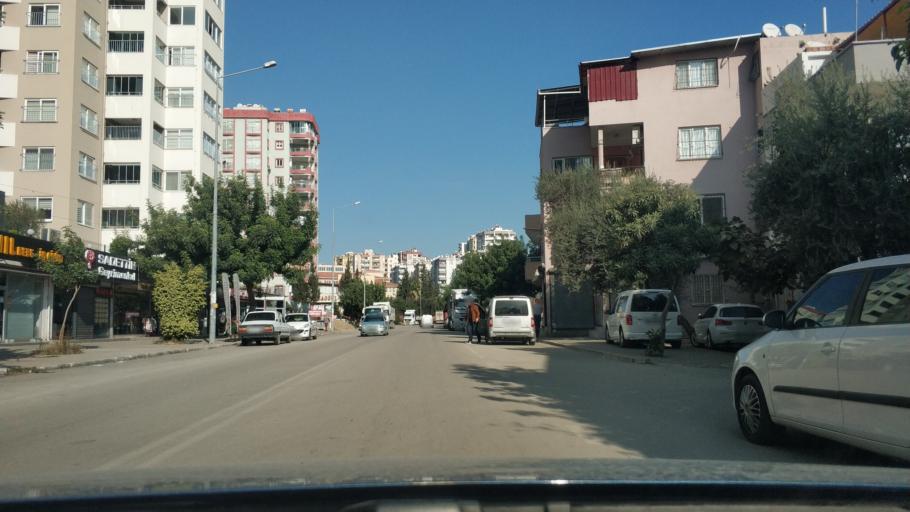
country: TR
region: Adana
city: Seyhan
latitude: 37.0204
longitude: 35.2912
